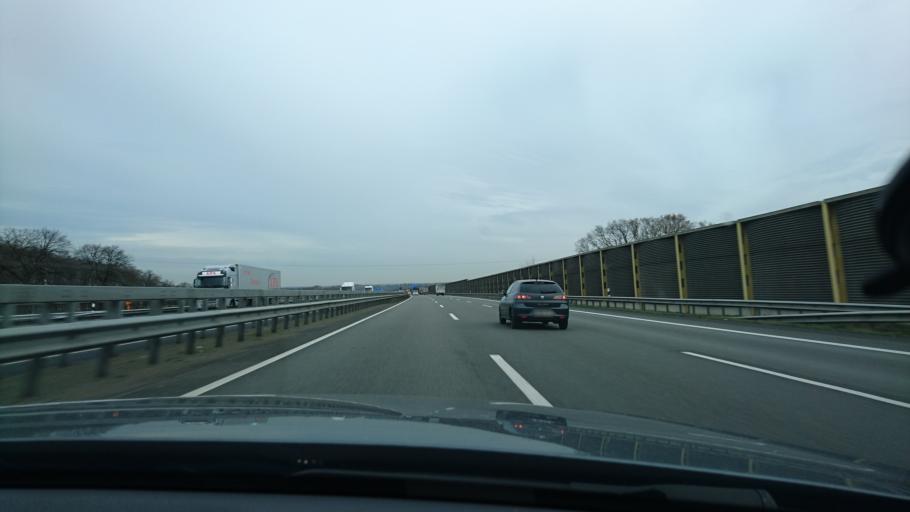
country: DE
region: Lower Saxony
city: Wallenhorst
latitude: 52.3765
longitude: 8.0439
